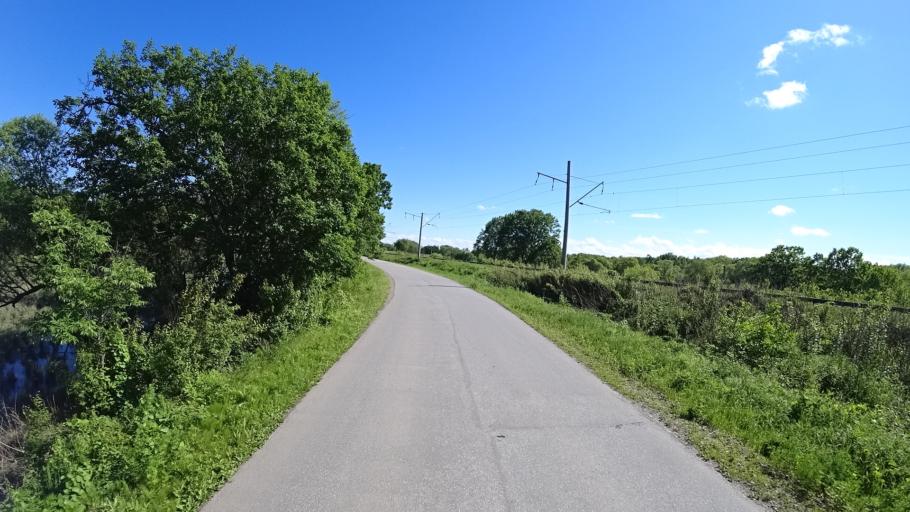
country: RU
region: Khabarovsk Krai
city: Khor
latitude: 47.8918
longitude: 135.0226
